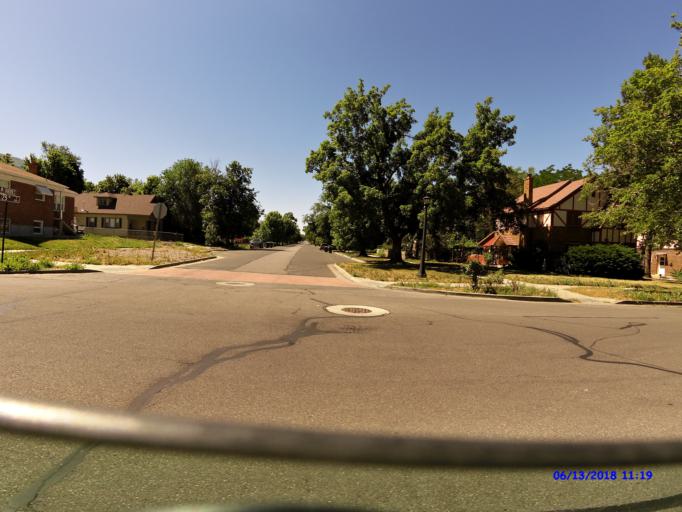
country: US
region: Utah
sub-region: Weber County
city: Ogden
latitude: 41.2204
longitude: -111.9510
